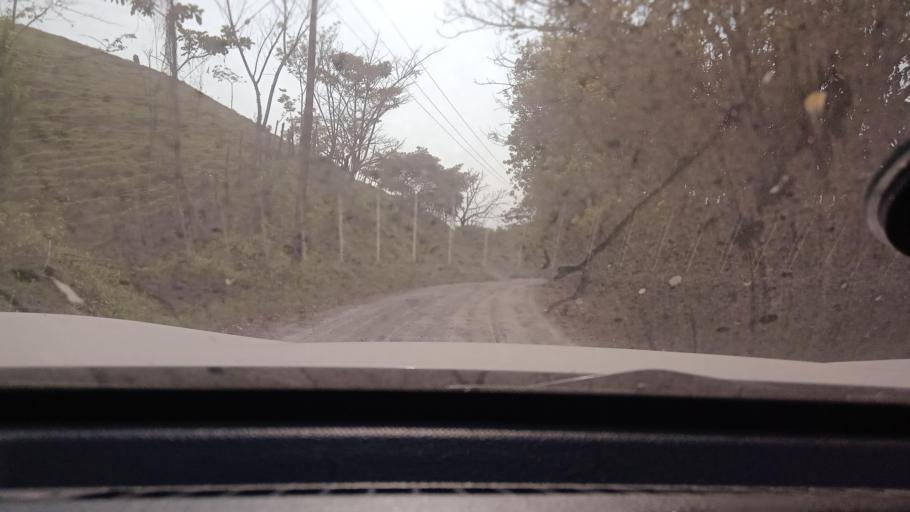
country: MX
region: Tabasco
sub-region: Huimanguillo
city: Francisco Rueda
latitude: 17.6203
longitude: -93.9462
